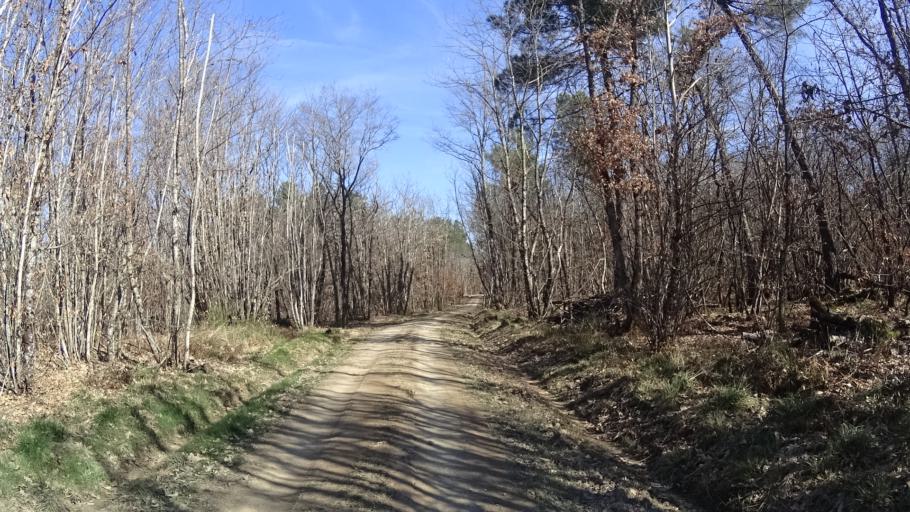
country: FR
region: Aquitaine
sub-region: Departement de la Dordogne
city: Riberac
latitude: 45.1925
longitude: 0.3079
